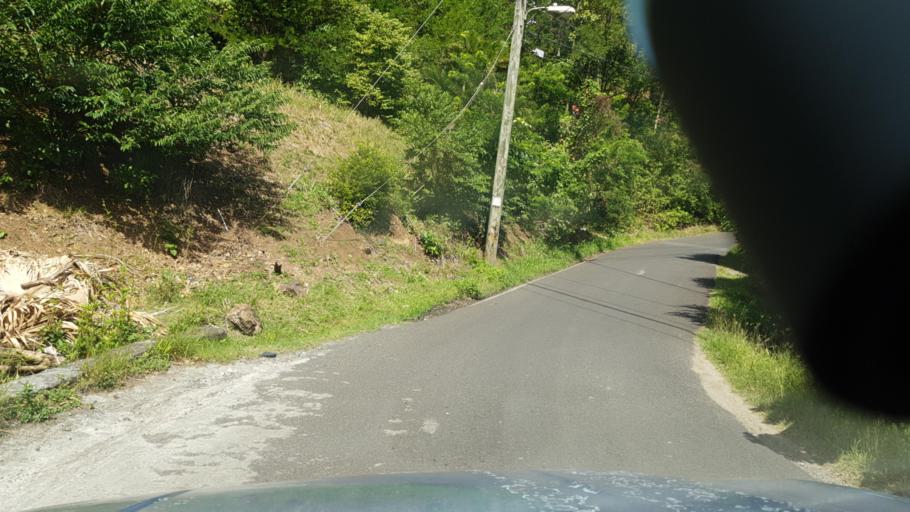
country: LC
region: Gros-Islet
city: Gros Islet
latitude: 14.0549
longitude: -60.9502
